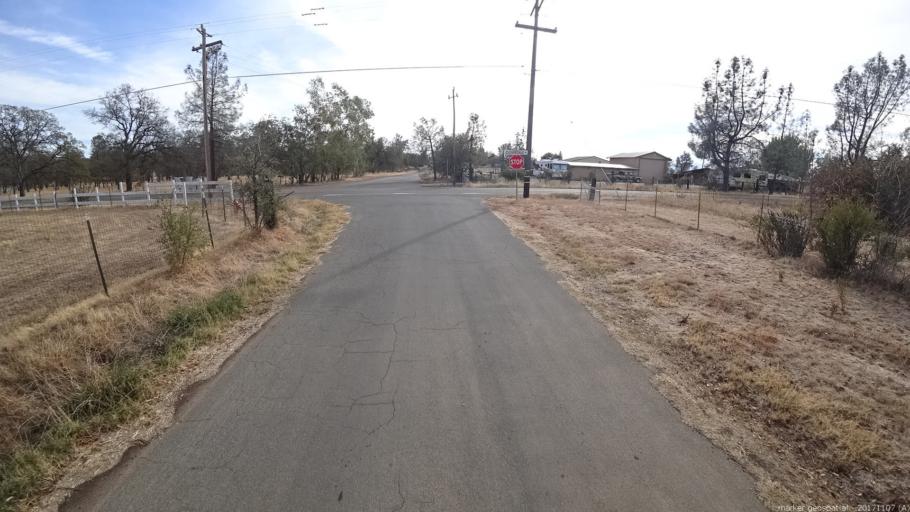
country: US
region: California
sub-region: Shasta County
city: Shasta
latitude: 40.4737
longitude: -122.4831
